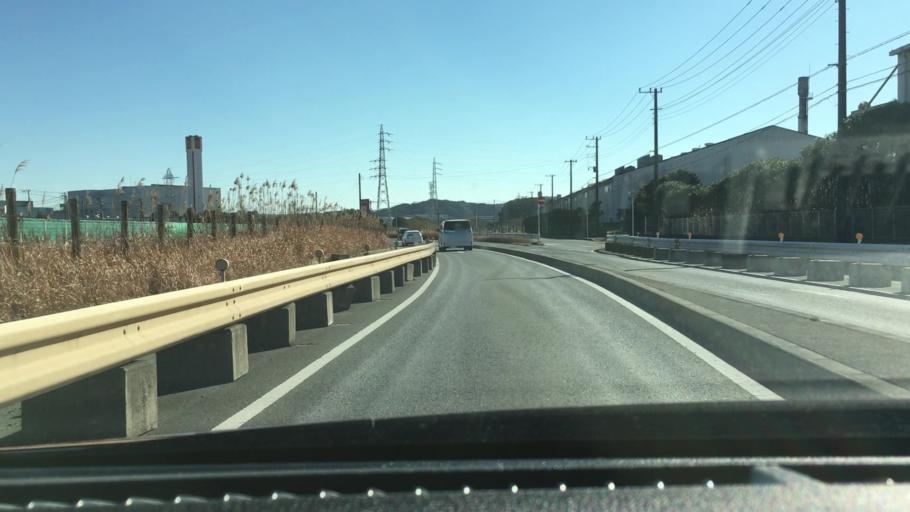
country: JP
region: Chiba
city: Kisarazu
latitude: 35.3727
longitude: 139.9077
